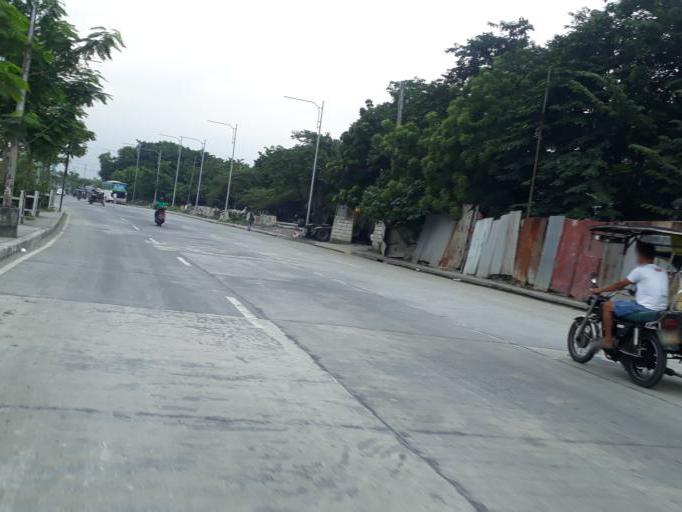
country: PH
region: Metro Manila
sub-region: Caloocan City
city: Niugan
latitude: 14.6491
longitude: 120.9491
